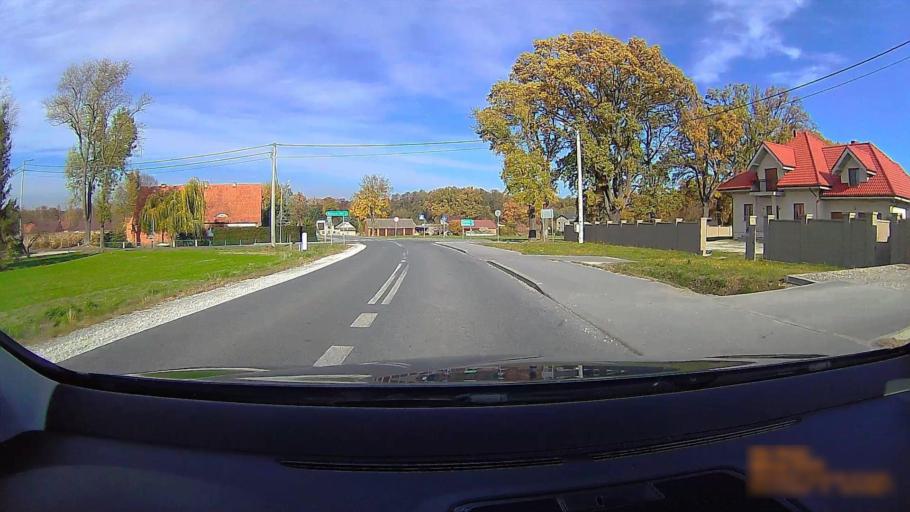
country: PL
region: Greater Poland Voivodeship
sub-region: Powiat ostrzeszowski
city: Doruchow
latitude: 51.3588
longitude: 18.0305
